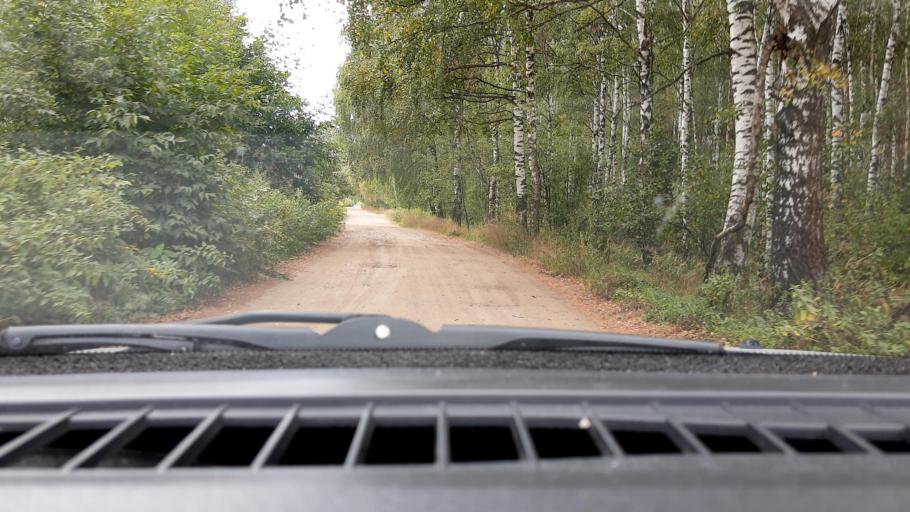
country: RU
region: Nizjnij Novgorod
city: Gorbatovka
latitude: 56.3107
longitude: 43.6949
